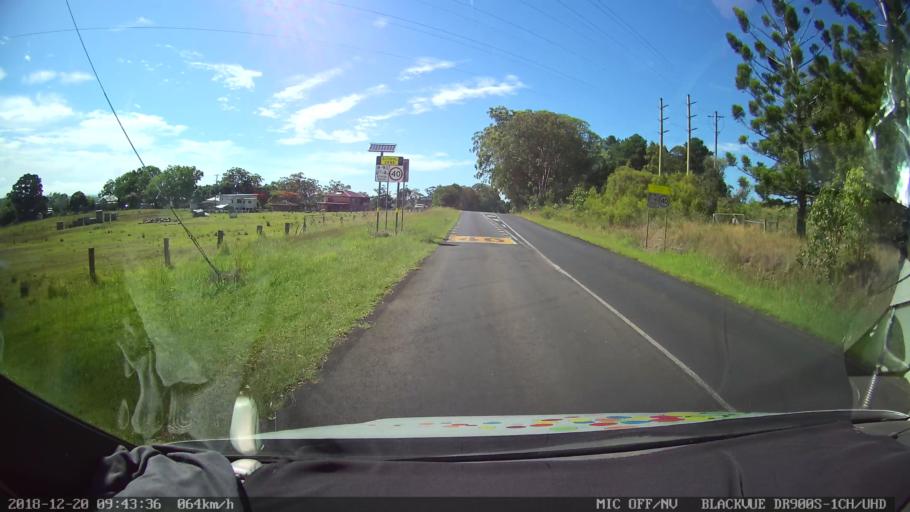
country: AU
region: New South Wales
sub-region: Lismore Municipality
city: Lismore
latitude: -28.7272
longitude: 153.2969
